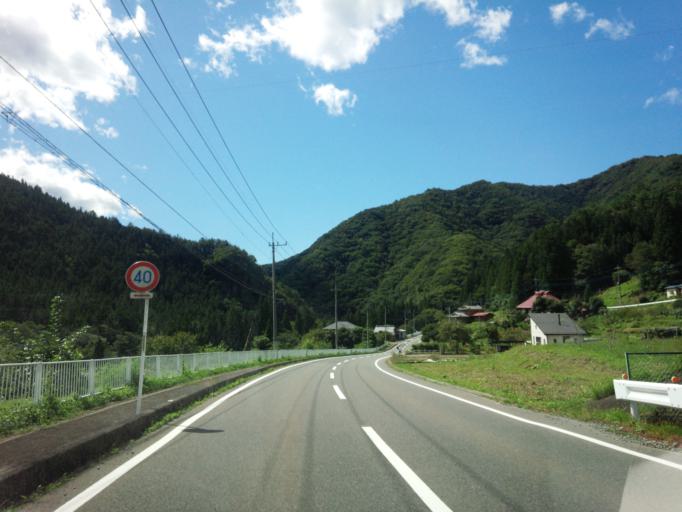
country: JP
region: Gunma
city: Nakanojomachi
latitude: 36.6470
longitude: 138.7968
